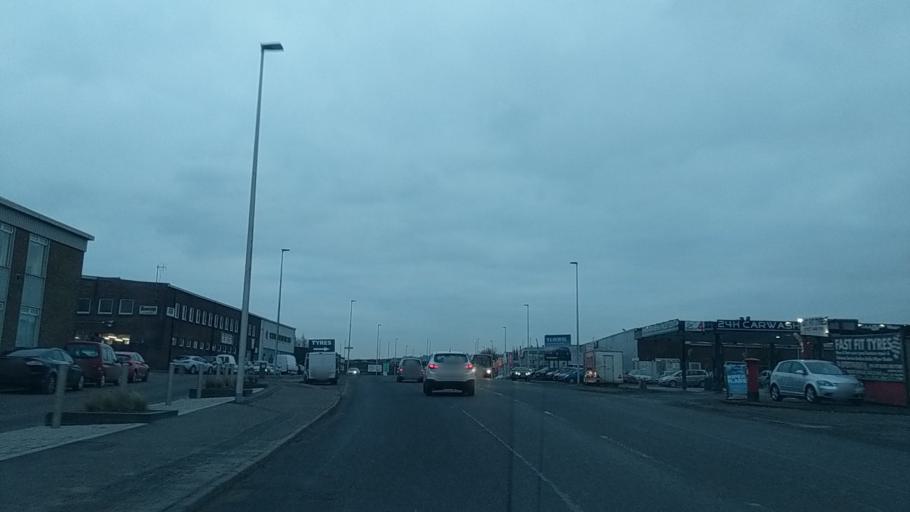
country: GB
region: Scotland
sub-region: South Lanarkshire
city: Rutherglen
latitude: 55.8350
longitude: -4.2257
